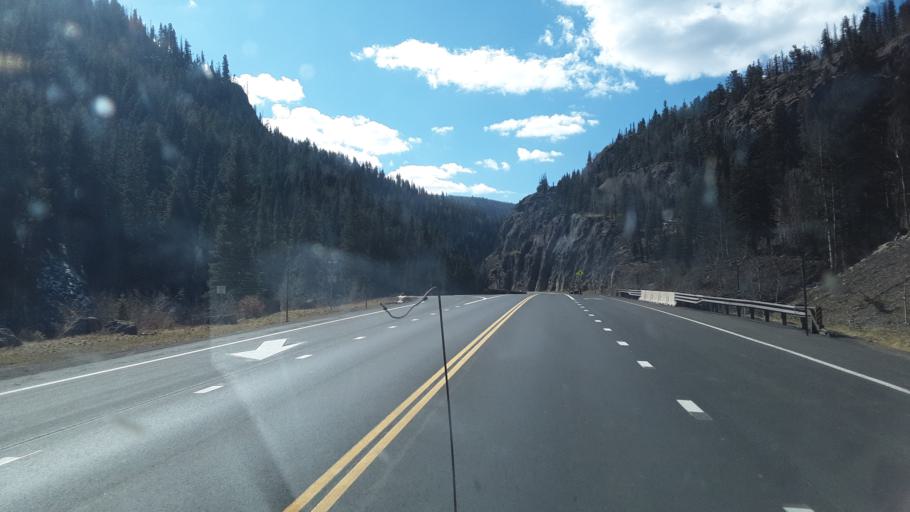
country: US
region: Colorado
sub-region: Mineral County
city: Creede
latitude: 37.5633
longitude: -106.7686
